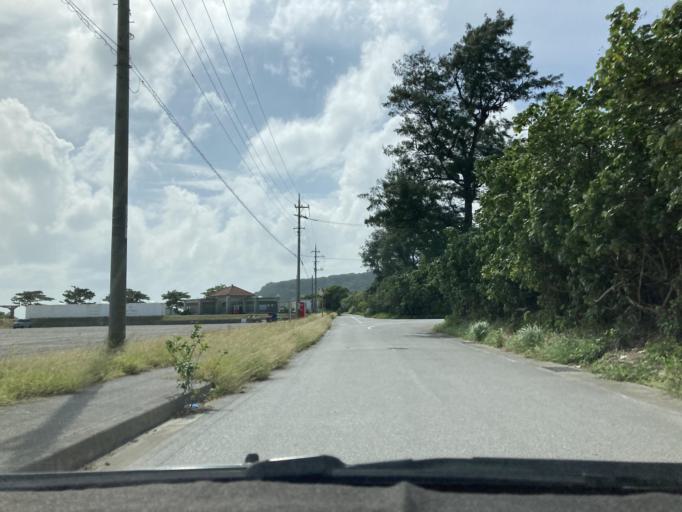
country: JP
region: Okinawa
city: Ginowan
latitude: 26.1488
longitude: 127.8049
